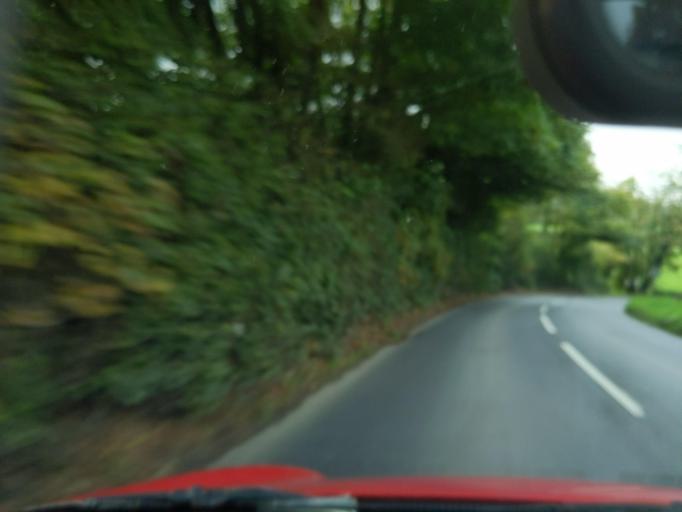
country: GB
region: England
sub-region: Devon
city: Great Torrington
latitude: 50.9332
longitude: -4.1525
